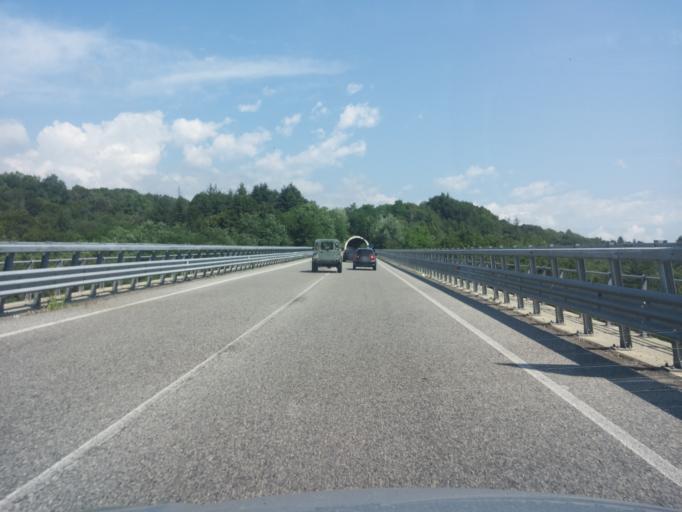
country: IT
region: Piedmont
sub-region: Provincia di Biella
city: Quaregna
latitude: 45.5932
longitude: 8.1706
